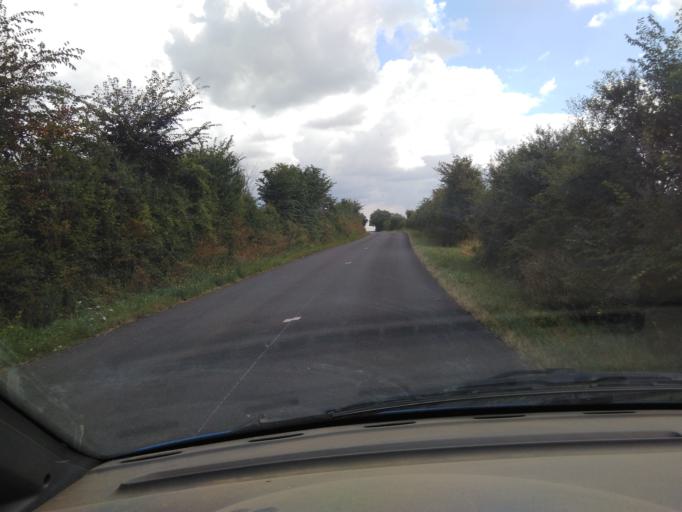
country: FR
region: Pays de la Loire
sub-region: Departement de la Vendee
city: Sainte-Hermine
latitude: 46.5539
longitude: -1.0311
